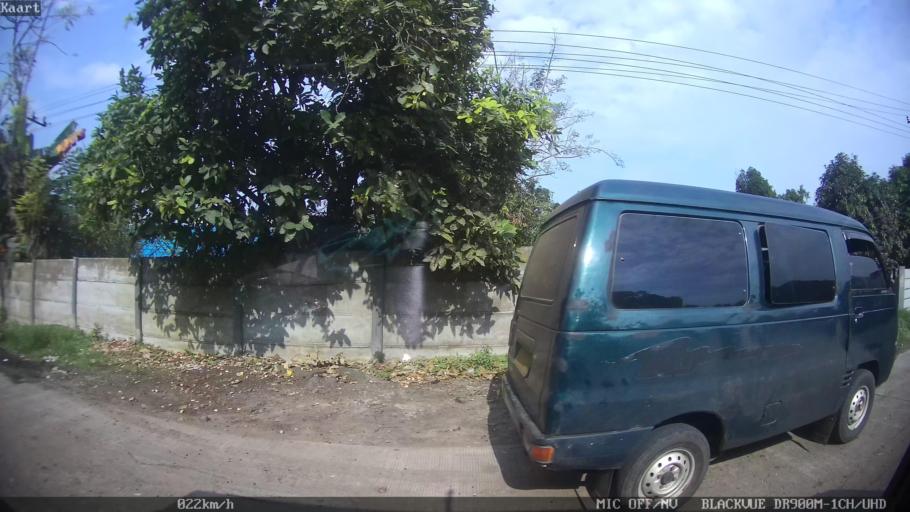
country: ID
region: Lampung
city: Panjang
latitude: -5.4807
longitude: 105.3258
